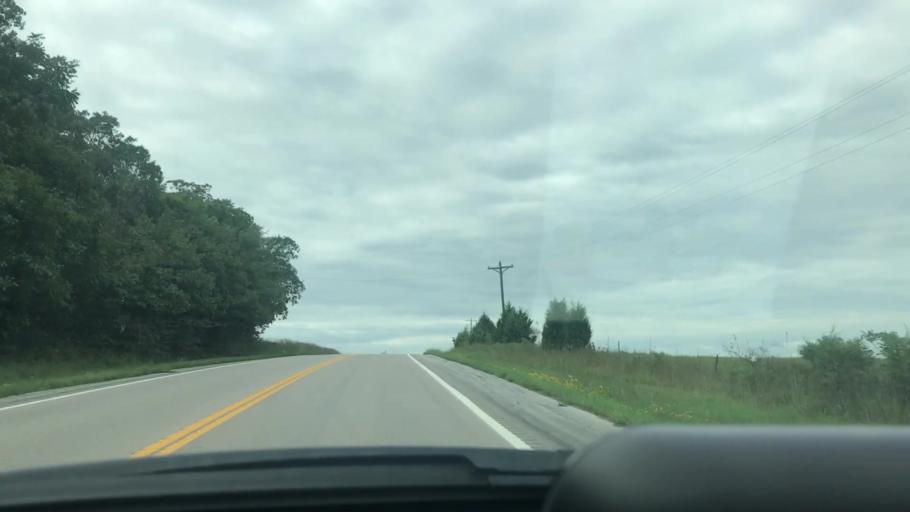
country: US
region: Missouri
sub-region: Benton County
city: Warsaw
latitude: 38.1429
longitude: -93.2887
